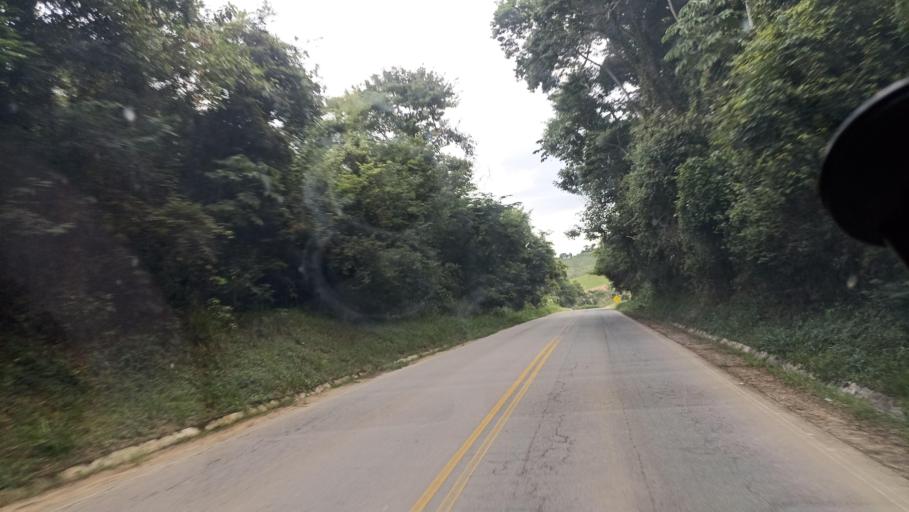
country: BR
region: Minas Gerais
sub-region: Cruzilia
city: Cruzilia
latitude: -21.8794
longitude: -44.8124
